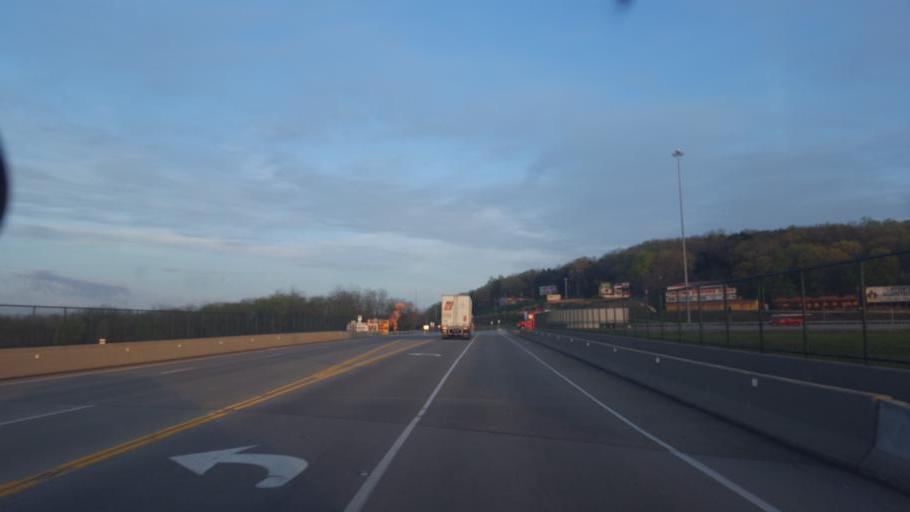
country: US
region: Kentucky
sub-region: Barren County
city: Cave City
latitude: 37.1354
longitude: -85.9775
